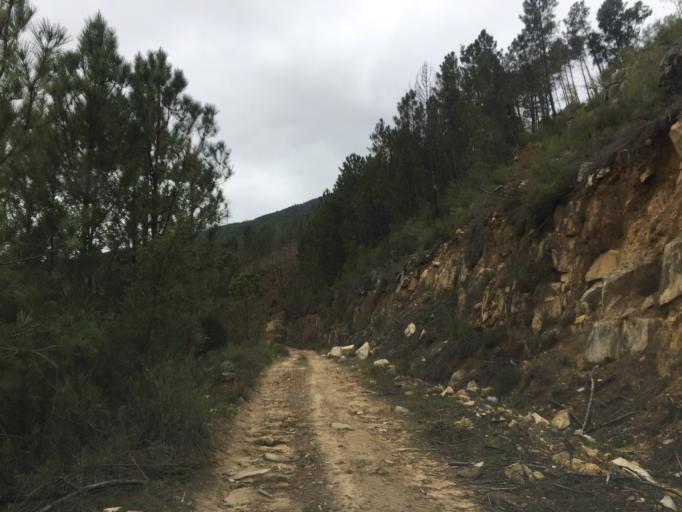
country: PT
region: Guarda
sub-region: Seia
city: Seia
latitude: 40.3183
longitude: -7.7296
